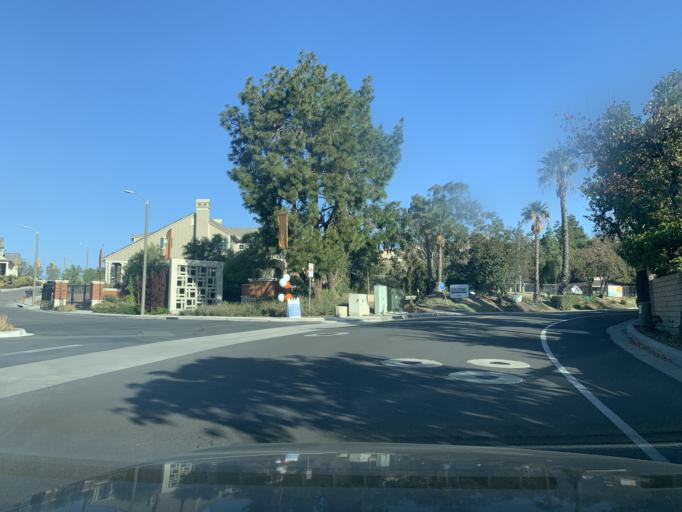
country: US
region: California
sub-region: Orange County
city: Villa Park
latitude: 33.8294
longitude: -117.8240
